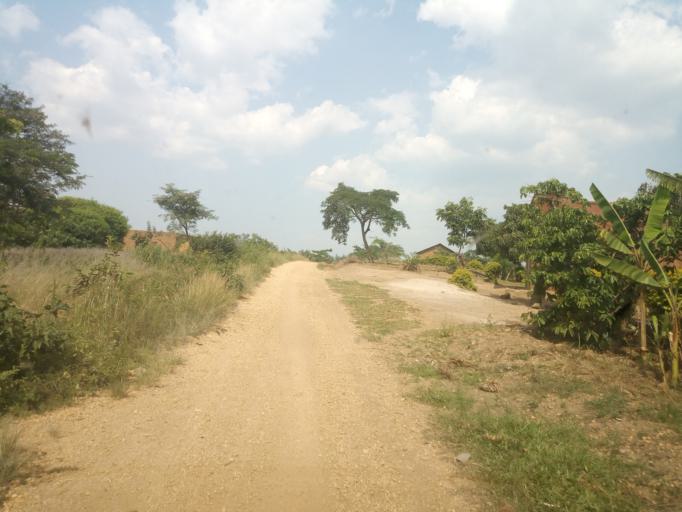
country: UG
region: Western Region
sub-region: Kanungu District
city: Ntungamo
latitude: -0.7905
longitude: 29.6581
